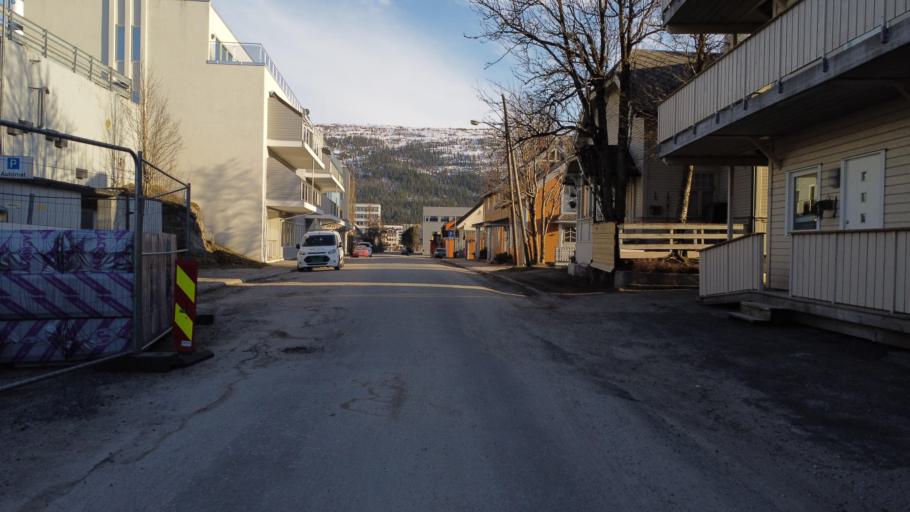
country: NO
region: Nordland
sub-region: Rana
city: Mo i Rana
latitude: 66.3148
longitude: 14.1319
